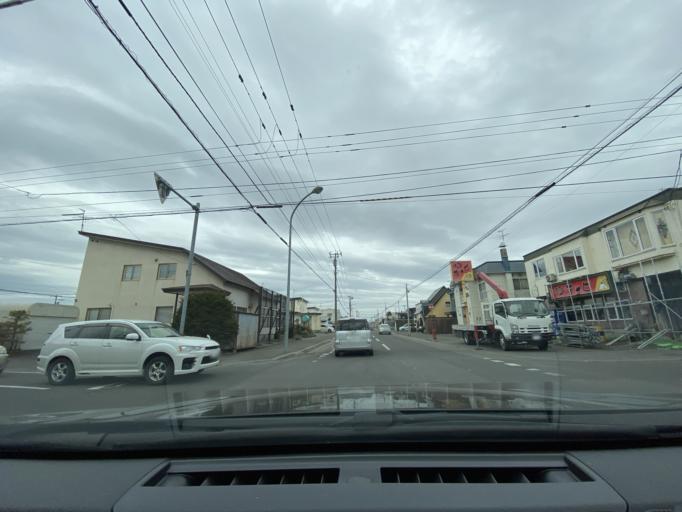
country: JP
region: Hokkaido
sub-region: Asahikawa-shi
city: Asahikawa
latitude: 43.7888
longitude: 142.4141
